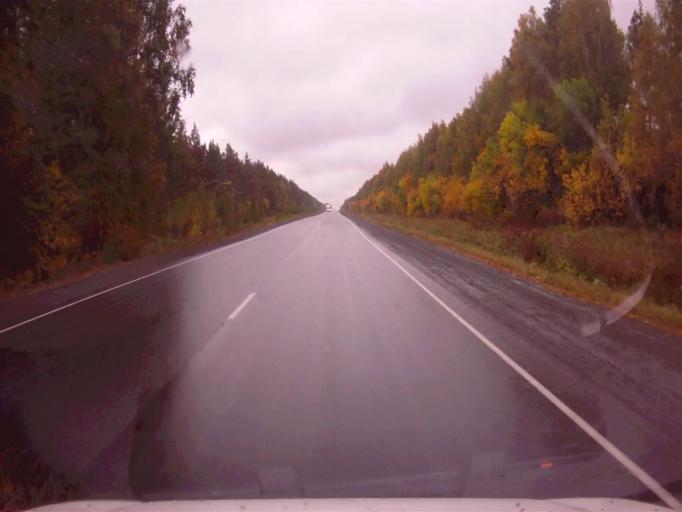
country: RU
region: Chelyabinsk
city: Roshchino
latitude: 55.3744
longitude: 61.1528
